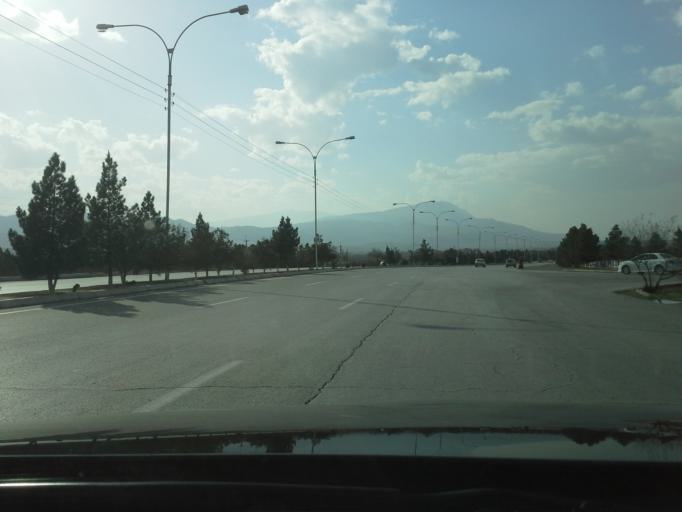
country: TM
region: Ahal
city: Abadan
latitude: 37.9711
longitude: 58.2634
